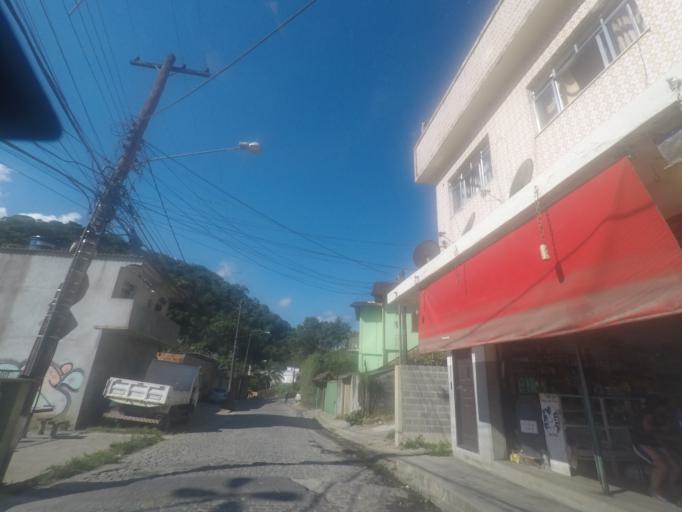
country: BR
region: Rio de Janeiro
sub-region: Petropolis
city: Petropolis
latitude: -22.5415
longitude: -43.2023
